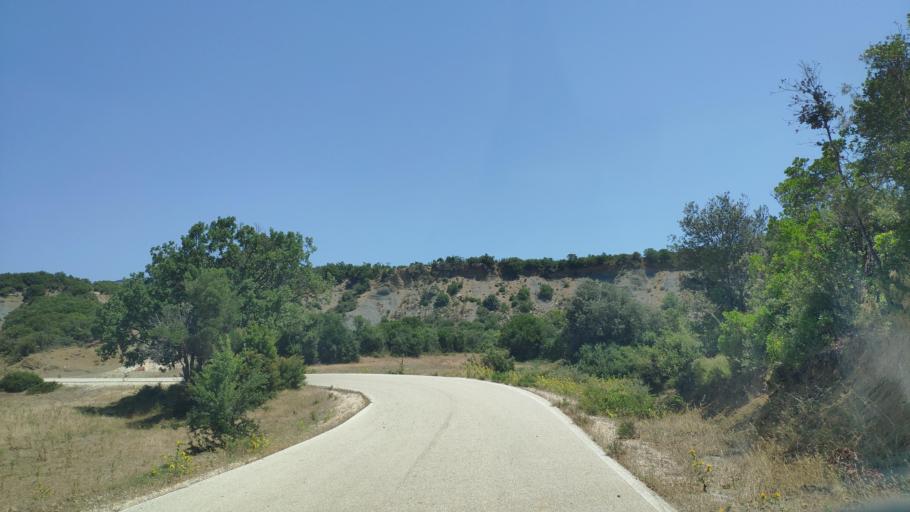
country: GR
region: West Greece
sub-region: Nomos Aitolias kai Akarnanias
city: Sardinia
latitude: 38.8743
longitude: 21.2802
